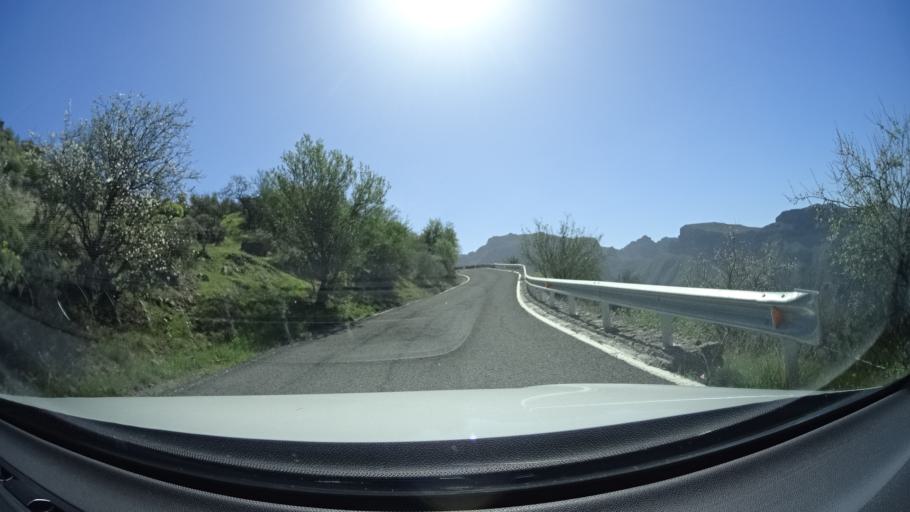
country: ES
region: Canary Islands
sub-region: Provincia de Las Palmas
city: Tejeda
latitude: 27.9890
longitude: -15.6394
